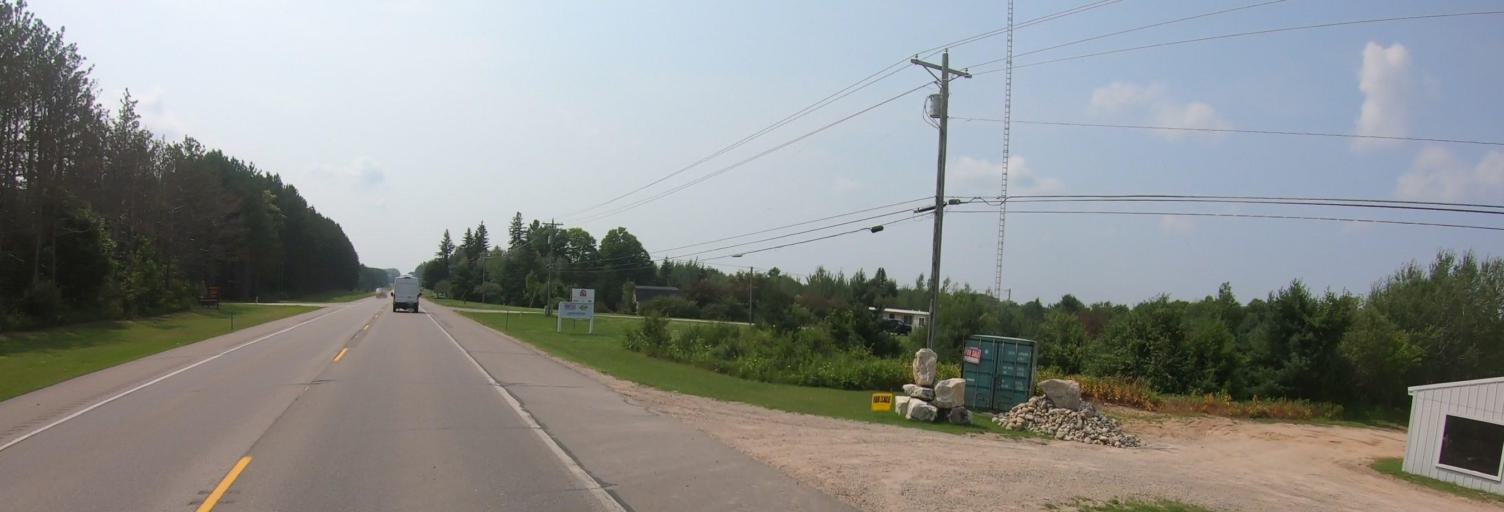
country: US
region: Michigan
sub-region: Luce County
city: Newberry
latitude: 46.3140
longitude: -85.5097
